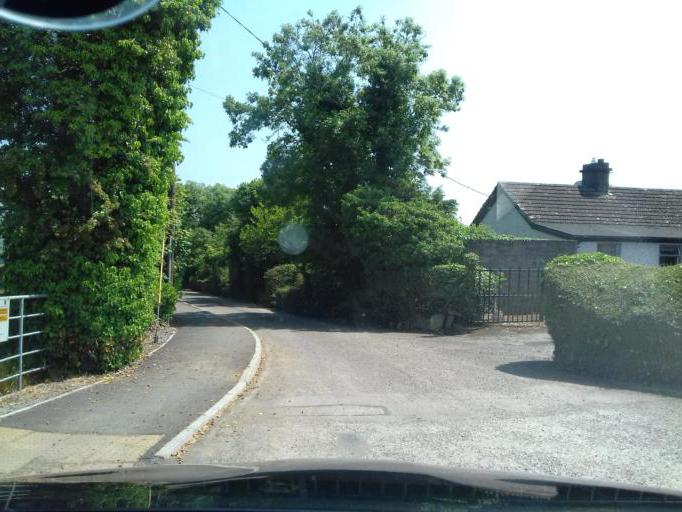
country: IE
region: Leinster
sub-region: An Mhi
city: Slane
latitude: 53.7174
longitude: -6.5400
